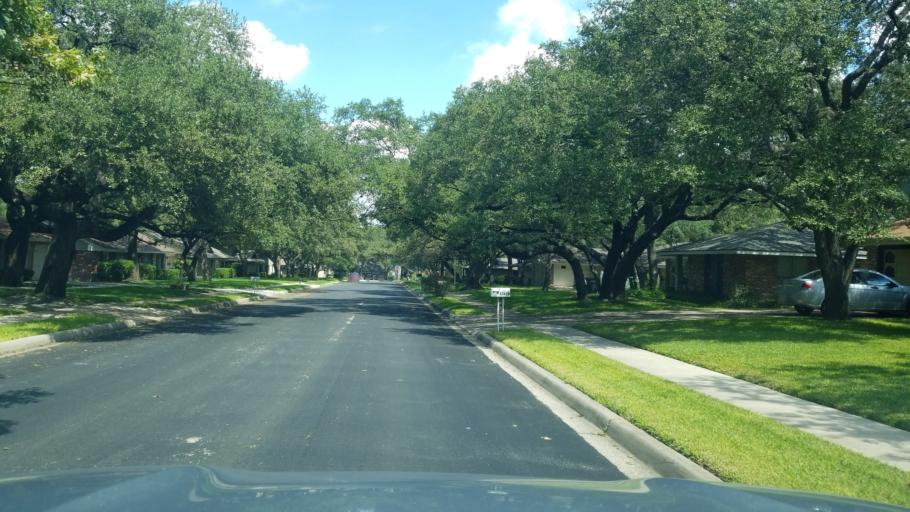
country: US
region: Texas
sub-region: Bexar County
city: Castle Hills
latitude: 29.5476
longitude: -98.5041
